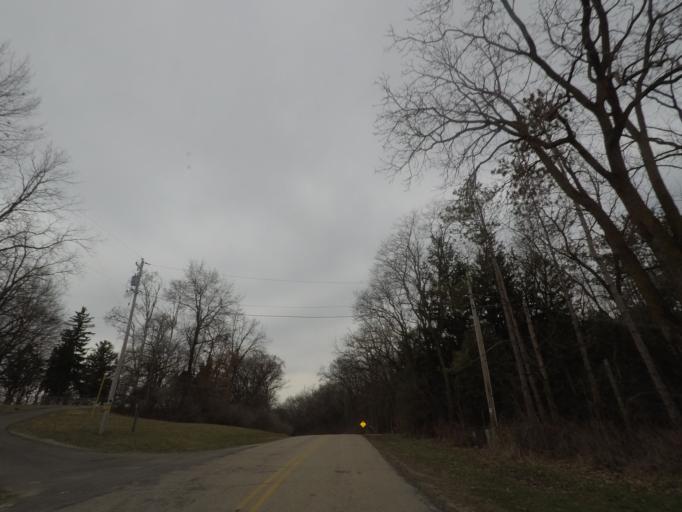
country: US
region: Wisconsin
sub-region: Dane County
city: Middleton
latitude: 43.1076
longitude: -89.5416
